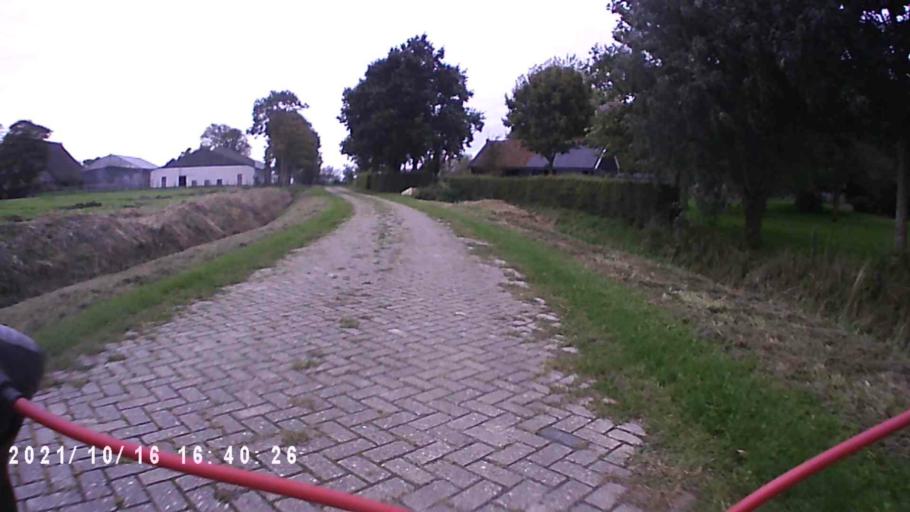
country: NL
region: Friesland
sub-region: Gemeente Dongeradeel
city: Anjum
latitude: 53.3775
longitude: 6.1466
